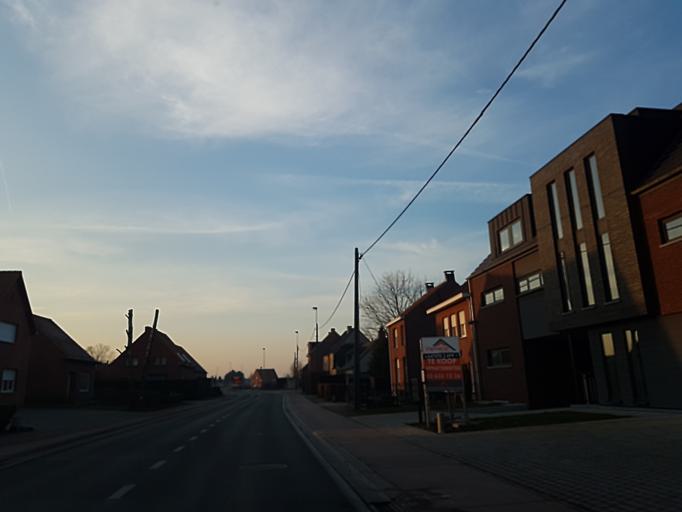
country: BE
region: Flanders
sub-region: Provincie Antwerpen
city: Brecht
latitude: 51.3516
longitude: 4.6552
